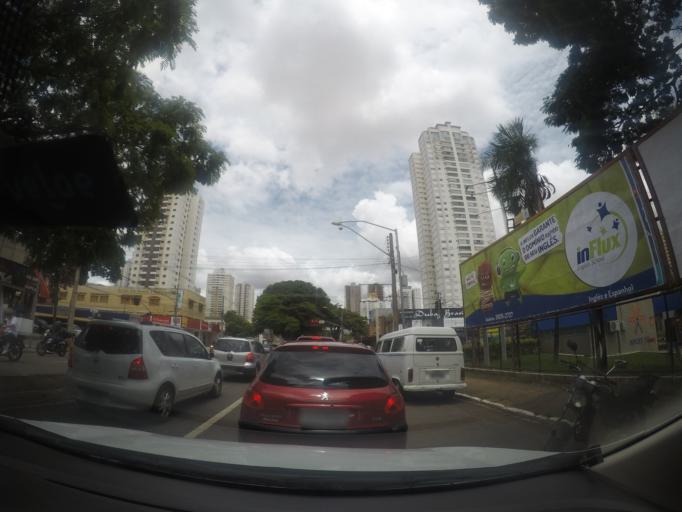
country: BR
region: Goias
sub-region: Goiania
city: Goiania
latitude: -16.6957
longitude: -49.2750
